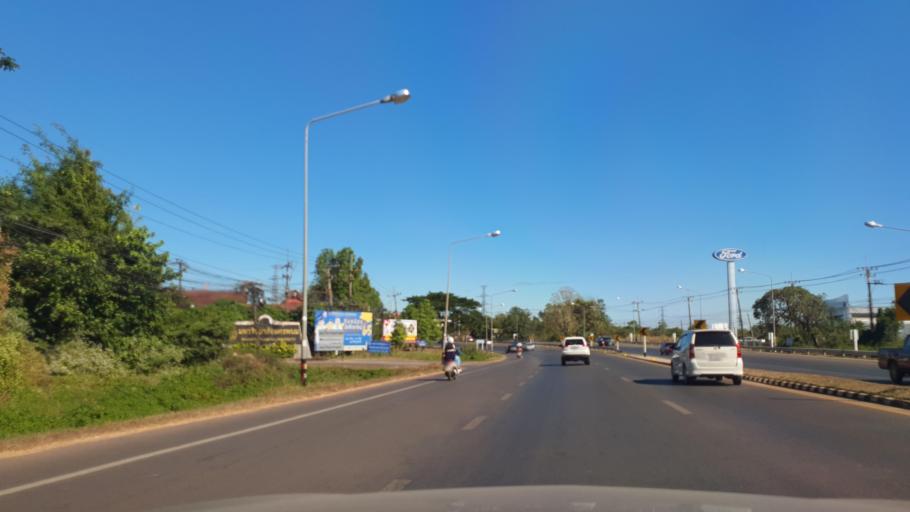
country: TH
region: Nakhon Phanom
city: Nakhon Phanom
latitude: 17.3825
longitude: 104.7548
